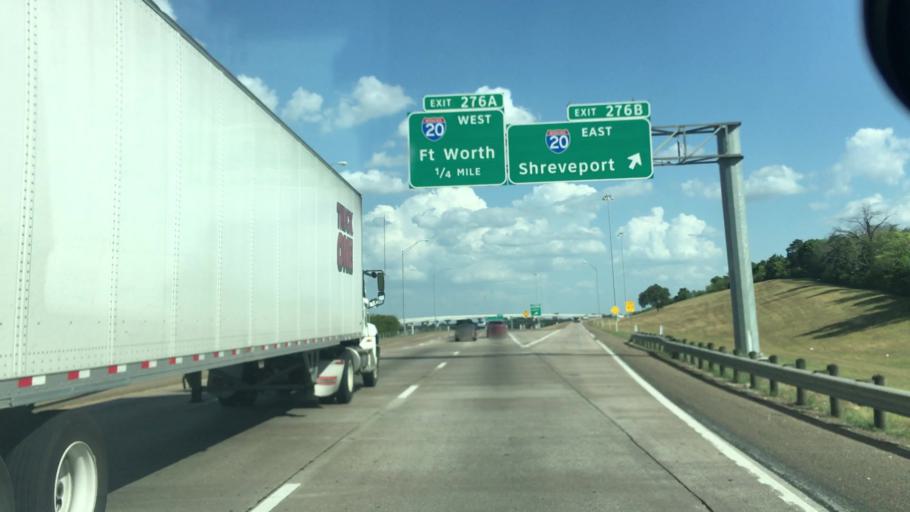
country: US
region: Texas
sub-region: Dallas County
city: Hutchins
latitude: 32.6674
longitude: -96.7320
